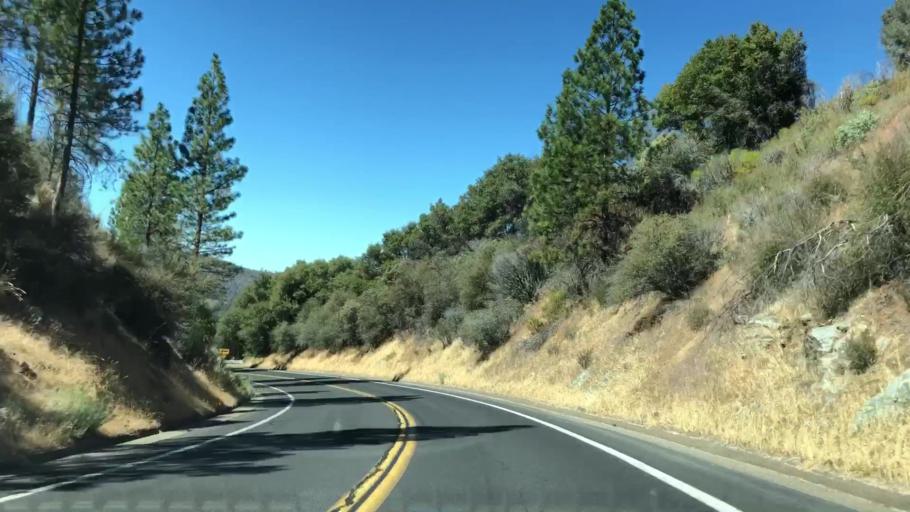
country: US
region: California
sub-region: Tuolumne County
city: Tuolumne City
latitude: 37.8294
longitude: -119.9833
